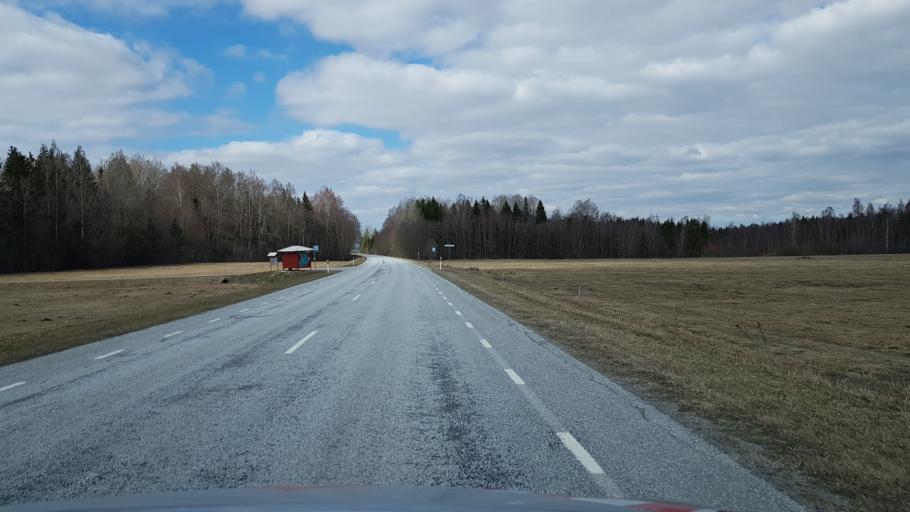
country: EE
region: Laeaene-Virumaa
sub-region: Rakke vald
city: Rakke
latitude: 58.9572
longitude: 26.1695
